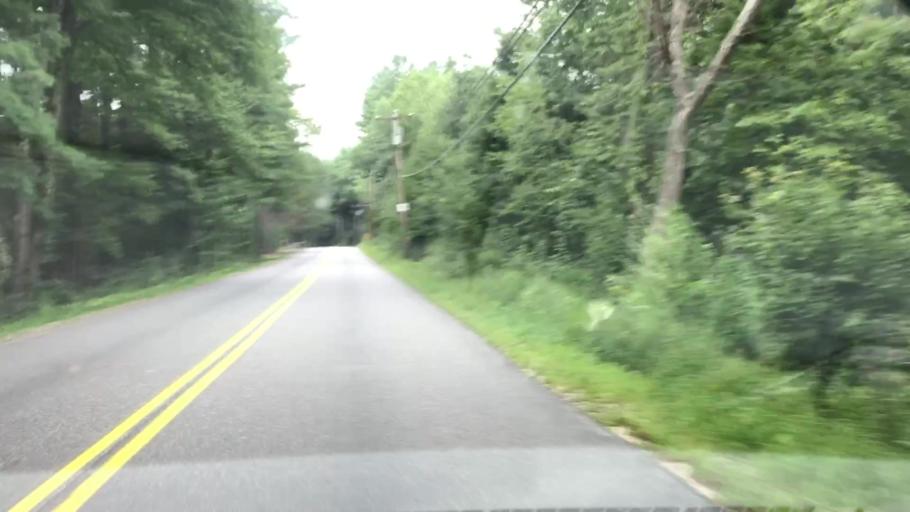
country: US
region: New Hampshire
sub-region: Hillsborough County
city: Milford
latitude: 42.8228
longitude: -71.5998
